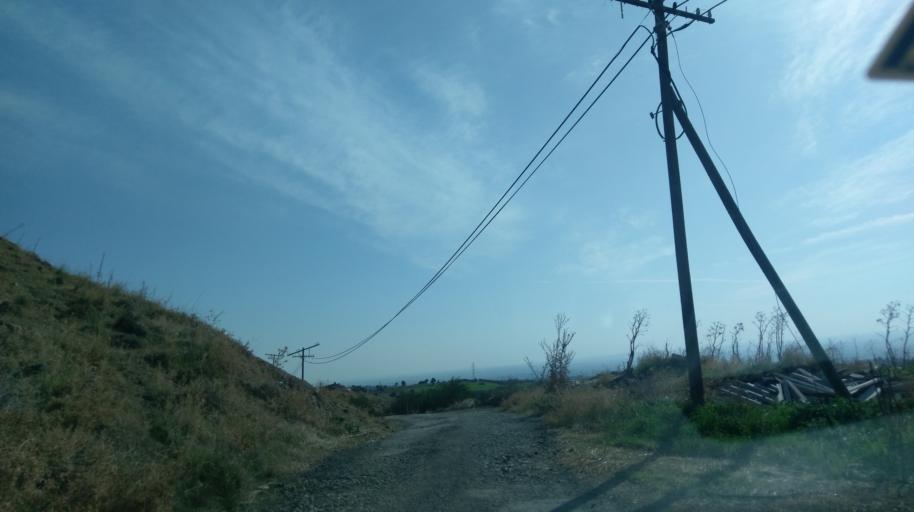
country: CY
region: Lefkosia
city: Nicosia
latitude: 35.2636
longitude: 33.4095
